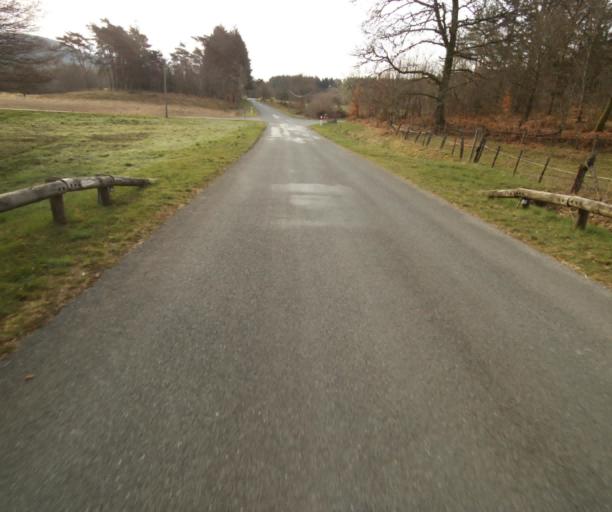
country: FR
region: Limousin
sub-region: Departement de la Correze
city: Treignac
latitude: 45.4725
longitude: 1.7973
